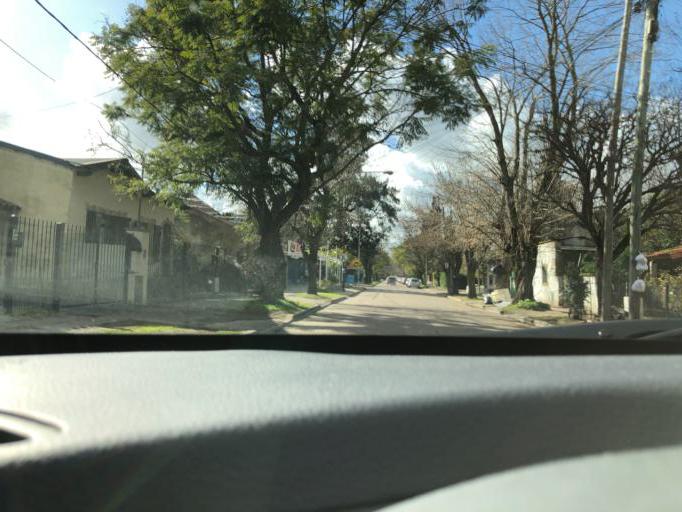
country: AR
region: Buenos Aires
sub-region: Partido de La Plata
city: La Plata
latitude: -34.8710
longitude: -58.0444
